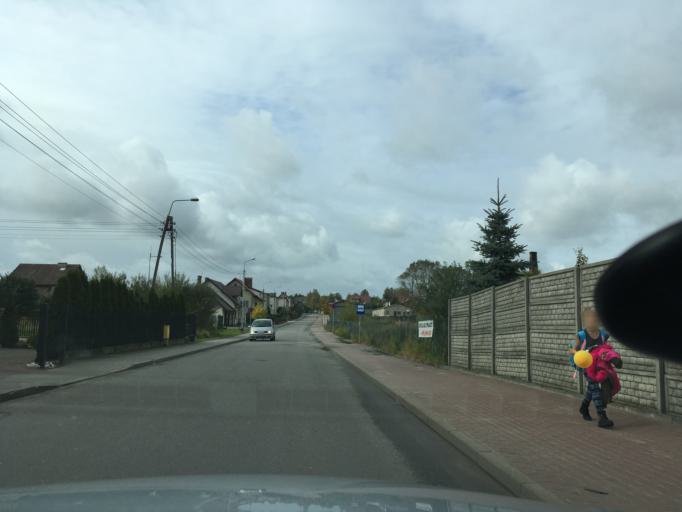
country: PL
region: Pomeranian Voivodeship
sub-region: Powiat koscierski
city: Koscierzyna
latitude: 54.1157
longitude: 17.9984
